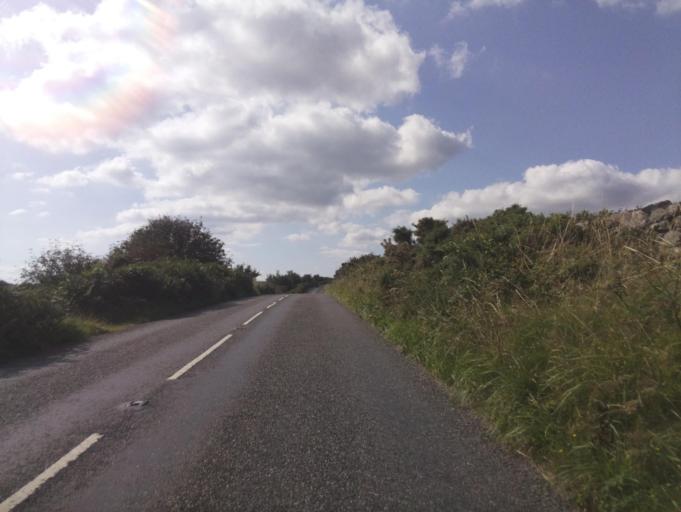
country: GB
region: England
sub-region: Devon
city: Buckfastleigh
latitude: 50.5476
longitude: -3.8966
